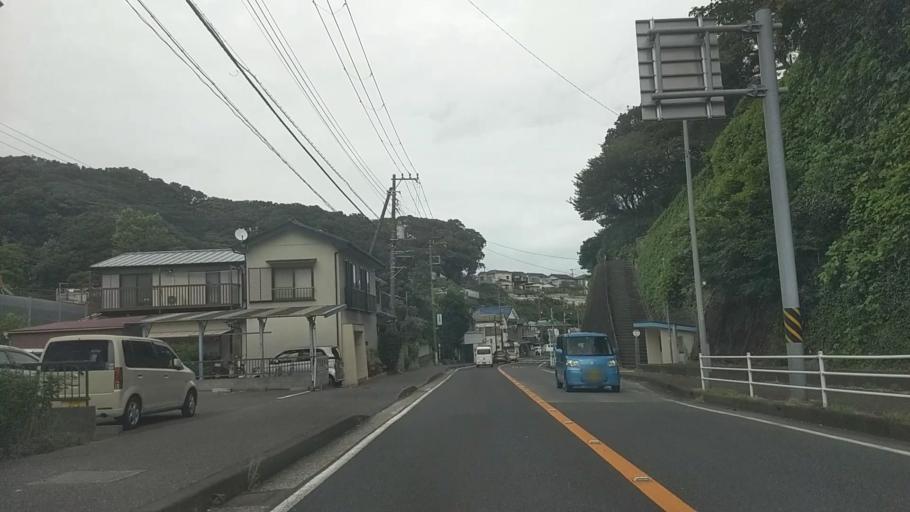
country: JP
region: Kanagawa
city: Yokosuka
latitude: 35.2456
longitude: 139.7248
